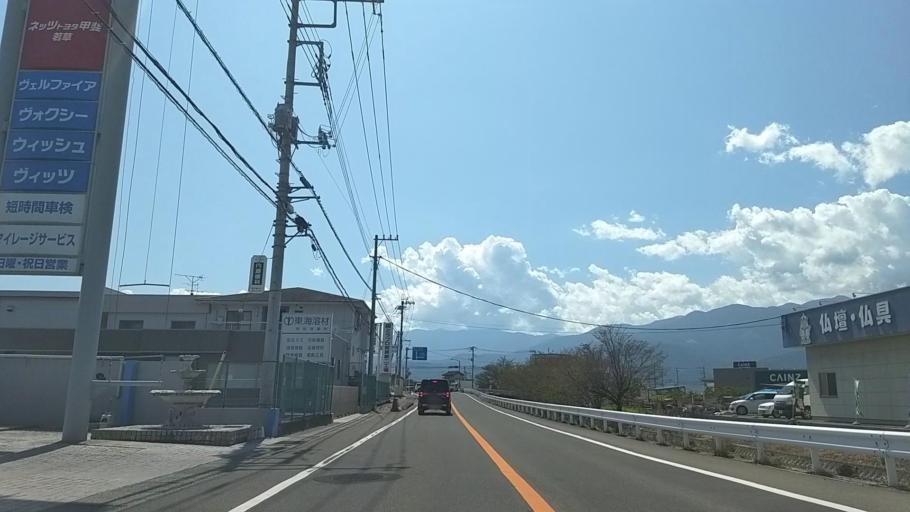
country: JP
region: Yamanashi
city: Ryuo
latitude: 35.5899
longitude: 138.4995
